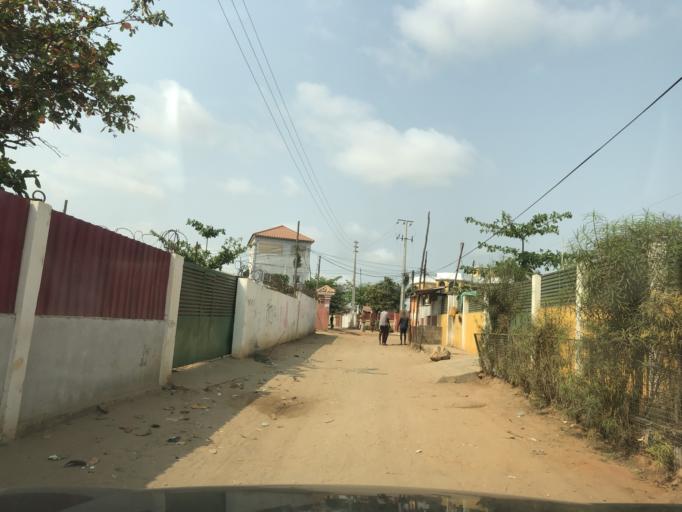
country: AO
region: Luanda
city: Luanda
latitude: -8.9027
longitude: 13.1666
